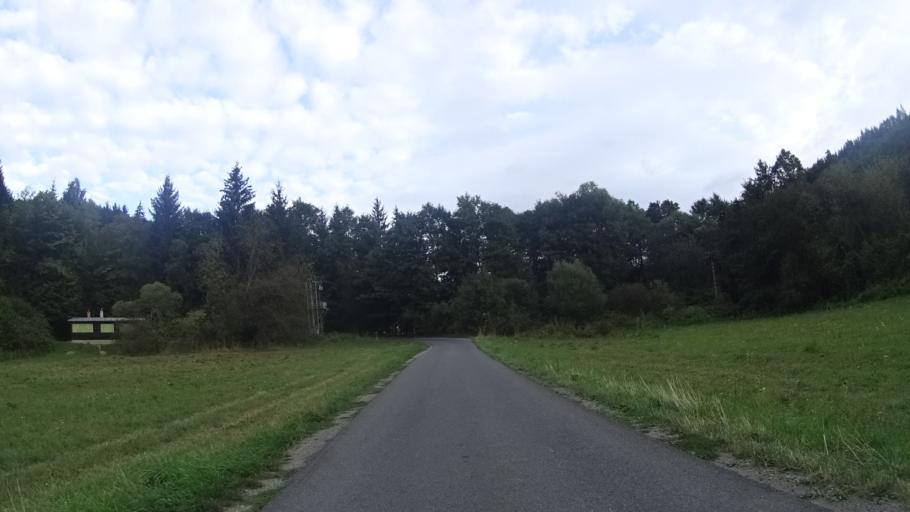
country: CZ
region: Olomoucky
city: Zabreh
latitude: 49.8674
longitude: 16.7913
